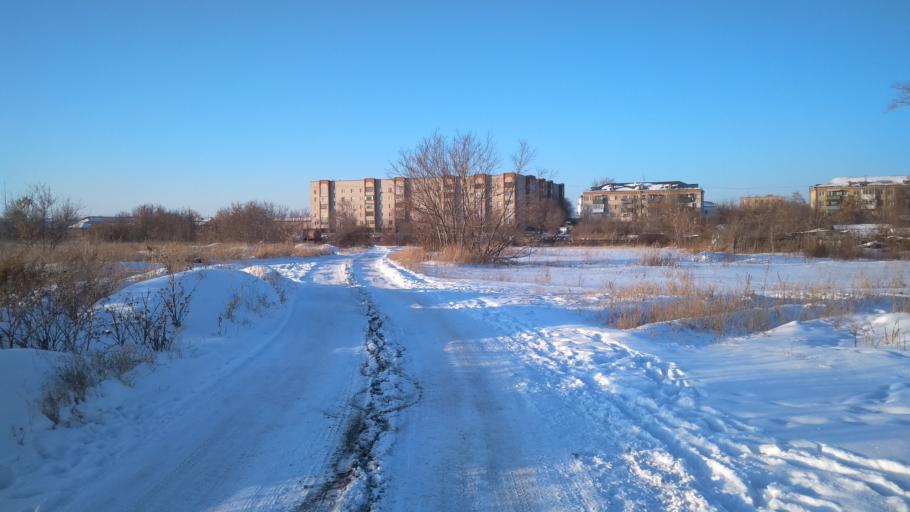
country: RU
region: Chelyabinsk
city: Troitsk
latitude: 54.0825
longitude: 61.5775
